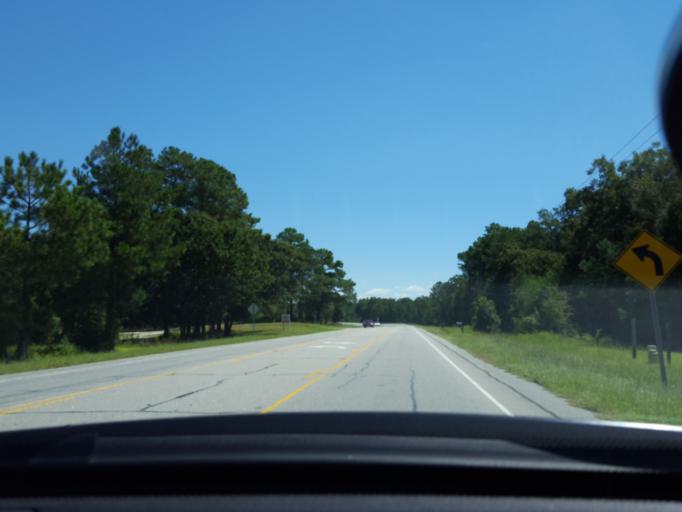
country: US
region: North Carolina
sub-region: Bladen County
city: Elizabethtown
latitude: 34.6476
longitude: -78.5633
